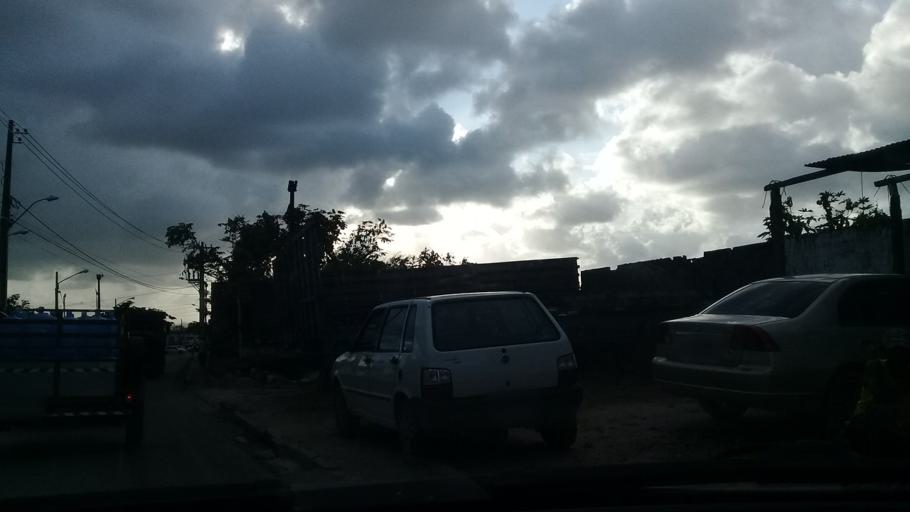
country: BR
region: Pernambuco
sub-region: Jaboatao Dos Guararapes
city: Jaboatao
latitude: -8.1387
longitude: -34.9456
